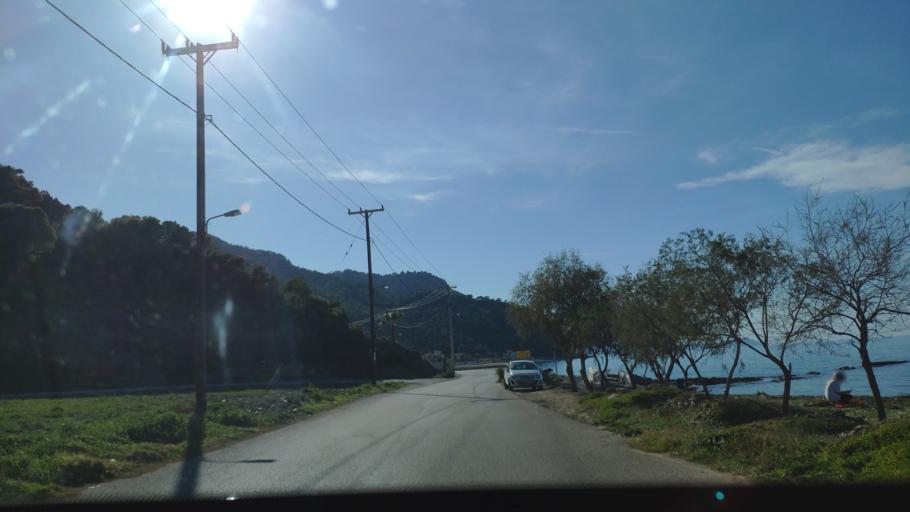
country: GR
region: Attica
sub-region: Nomarchia Dytikis Attikis
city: Kineta
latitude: 38.0669
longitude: 23.1464
